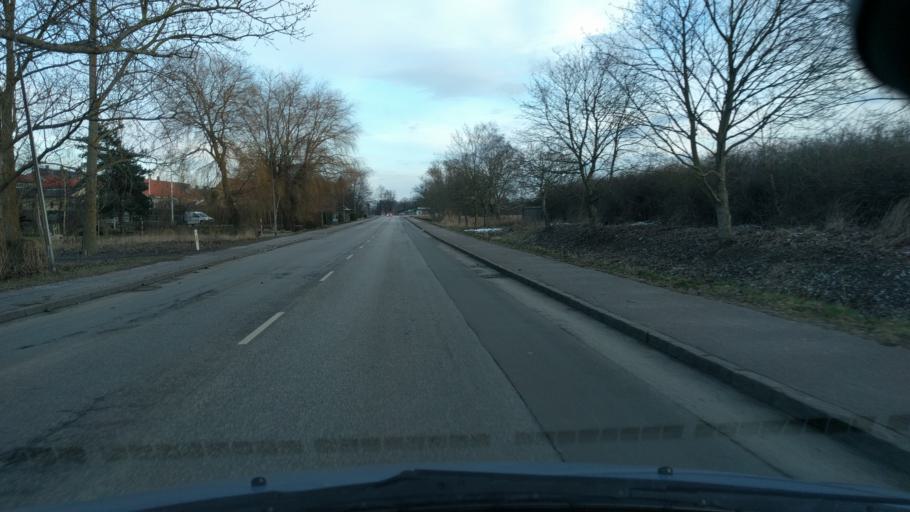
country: DK
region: Zealand
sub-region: Guldborgsund Kommune
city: Stubbekobing
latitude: 54.8884
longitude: 12.0443
